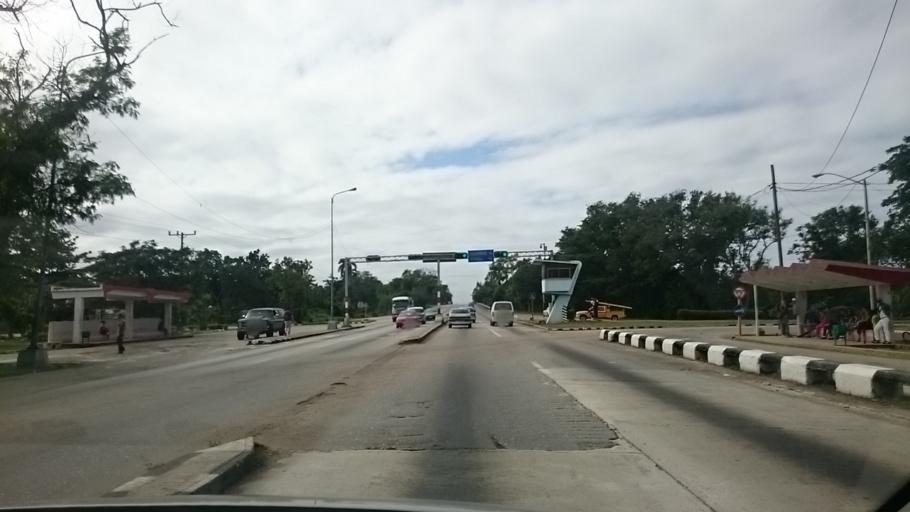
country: CU
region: La Habana
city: Alamar
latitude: 23.1561
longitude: -82.2704
